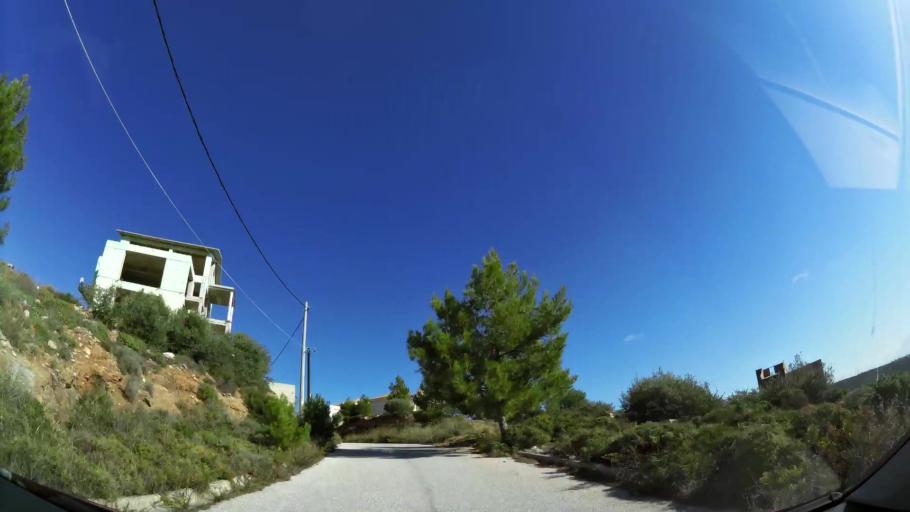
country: GR
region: Attica
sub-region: Nomarchia Anatolikis Attikis
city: Dhrafi
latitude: 38.0327
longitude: 23.8988
